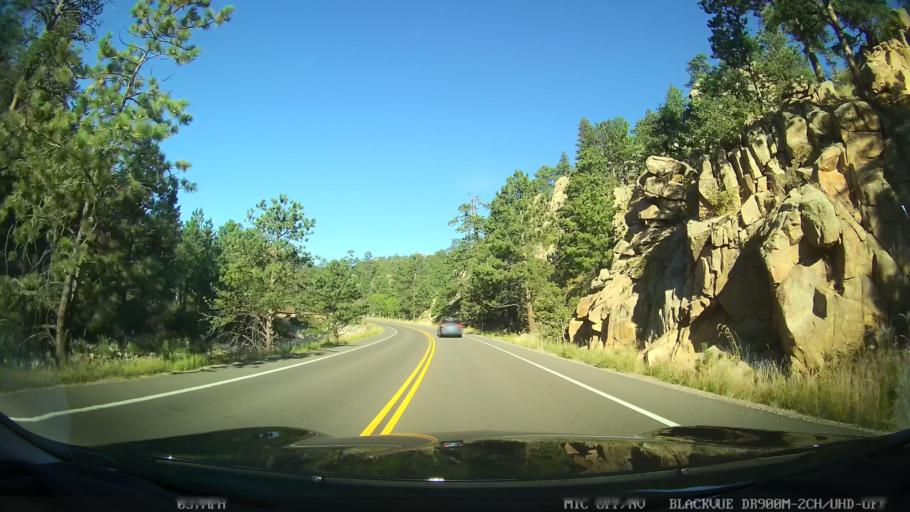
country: US
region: Colorado
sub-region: Larimer County
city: Estes Park
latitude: 40.3912
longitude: -105.4586
